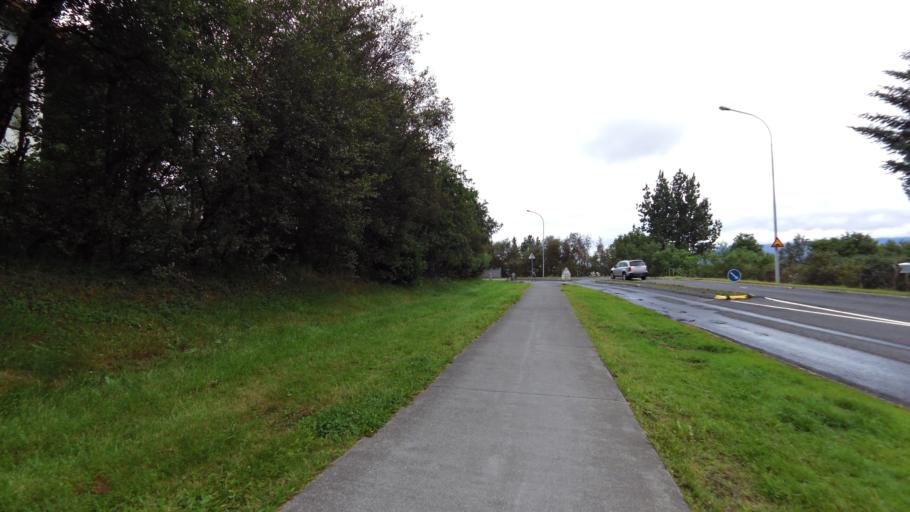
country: IS
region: Capital Region
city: Reykjavik
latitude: 64.1218
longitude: -21.8541
